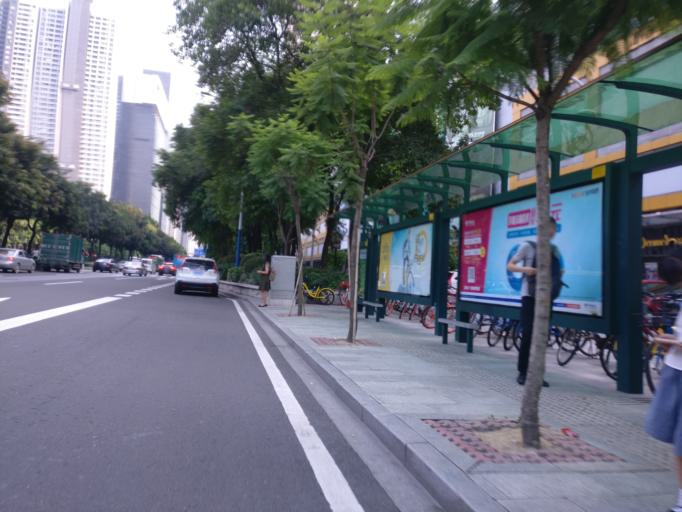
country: CN
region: Guangdong
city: Wushan
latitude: 23.1286
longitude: 113.3224
